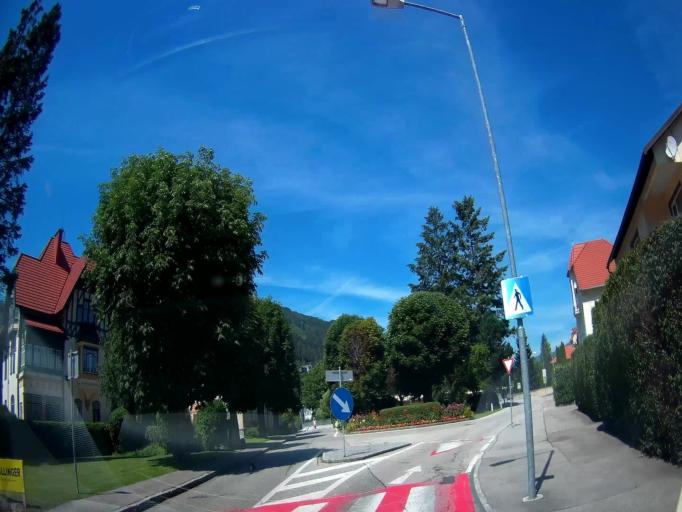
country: AT
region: Carinthia
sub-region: Politischer Bezirk Sankt Veit an der Glan
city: Friesach
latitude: 46.9515
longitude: 14.4118
